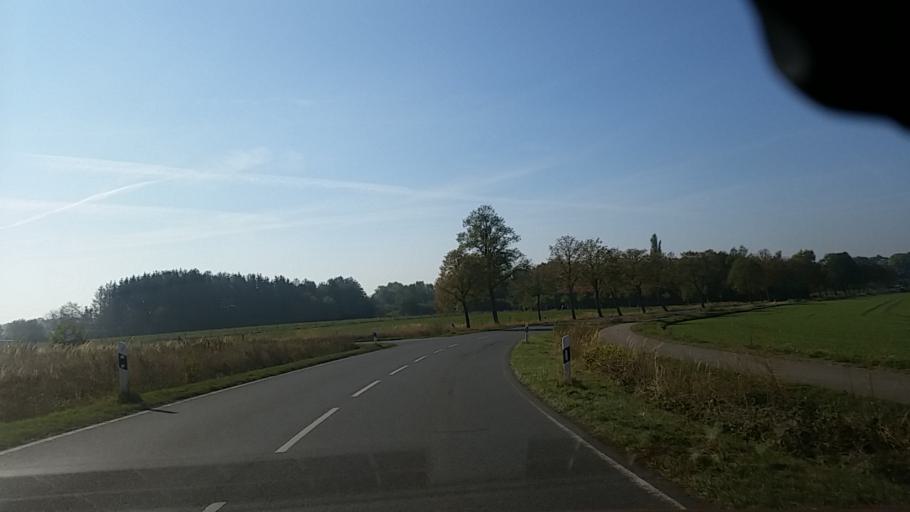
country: DE
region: Lower Saxony
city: Wolfsburg
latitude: 52.4046
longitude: 10.8418
